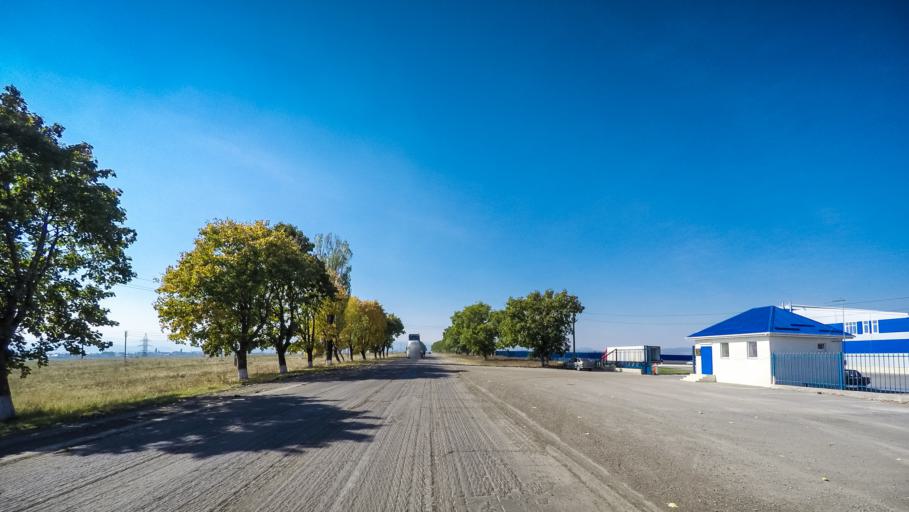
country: RU
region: Kabardino-Balkariya
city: Chegem Vtoroy
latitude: 43.5765
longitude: 43.5674
